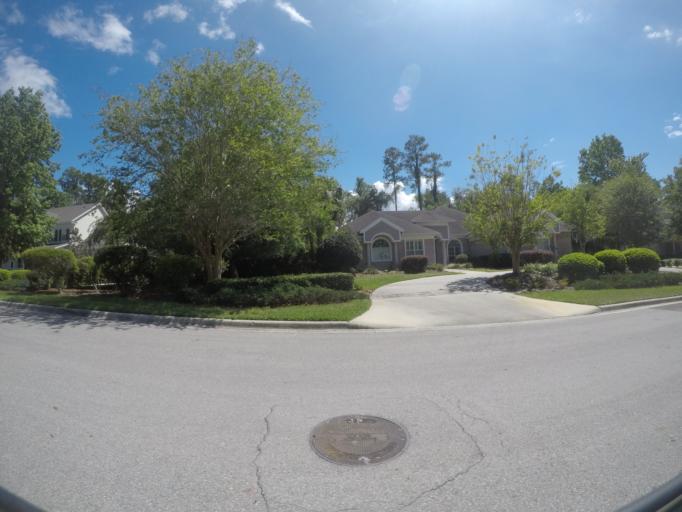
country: US
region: Florida
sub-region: Alachua County
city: Gainesville
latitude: 29.6167
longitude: -82.4343
